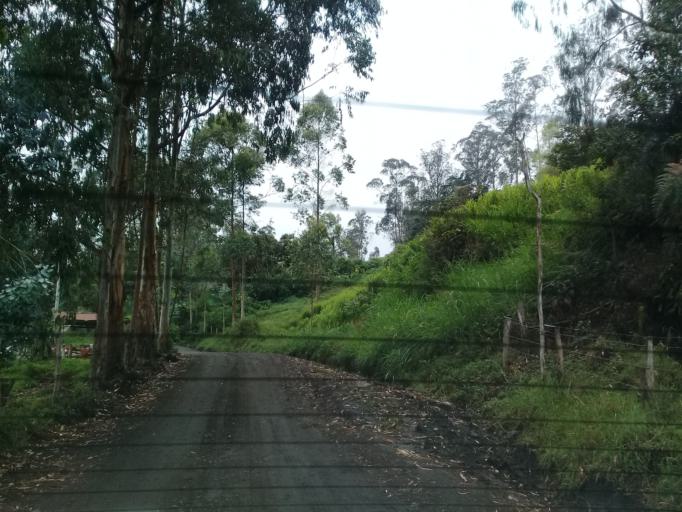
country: CO
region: Cundinamarca
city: Caqueza
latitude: 4.3965
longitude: -73.9833
